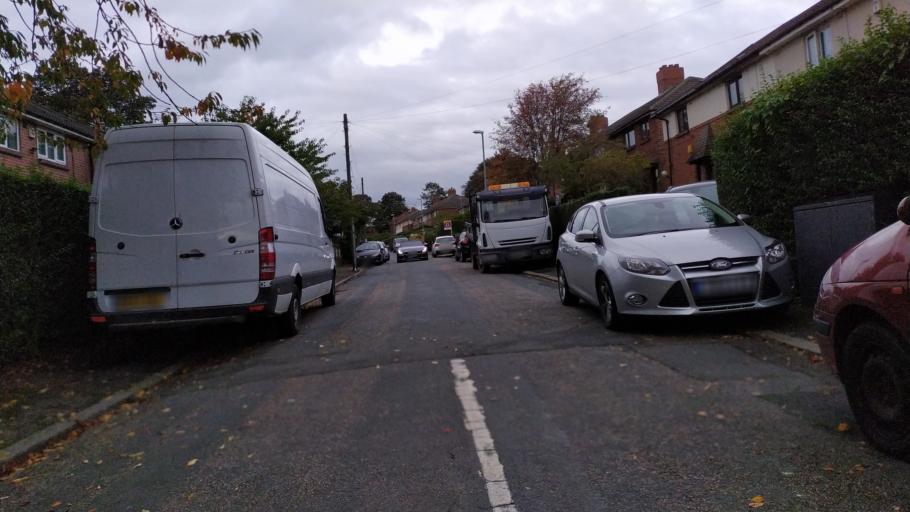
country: GB
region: England
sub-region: City and Borough of Leeds
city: Chapel Allerton
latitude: 53.8251
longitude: -1.5492
